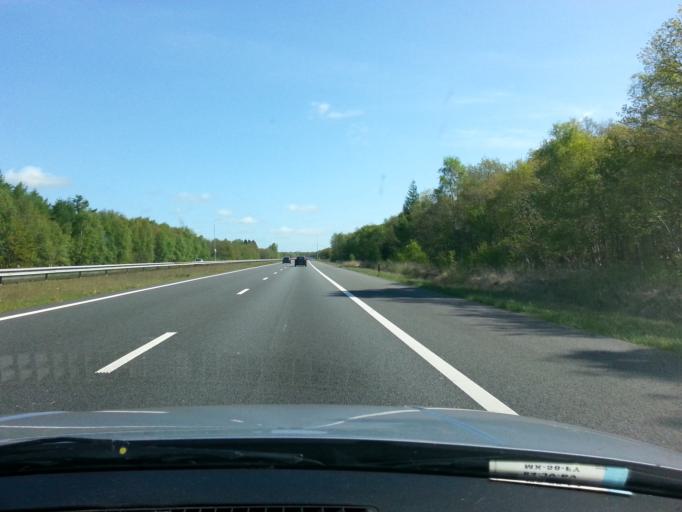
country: NL
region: Friesland
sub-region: Gemeente Smallingerland
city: Boornbergum
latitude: 53.0745
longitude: 6.0647
